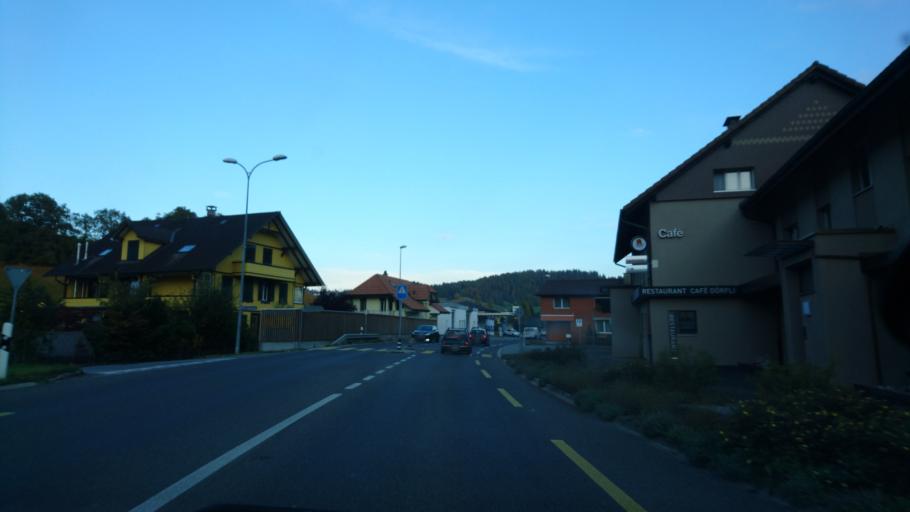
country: CH
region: Bern
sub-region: Bern-Mittelland District
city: Bowil
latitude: 46.9003
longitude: 7.6947
